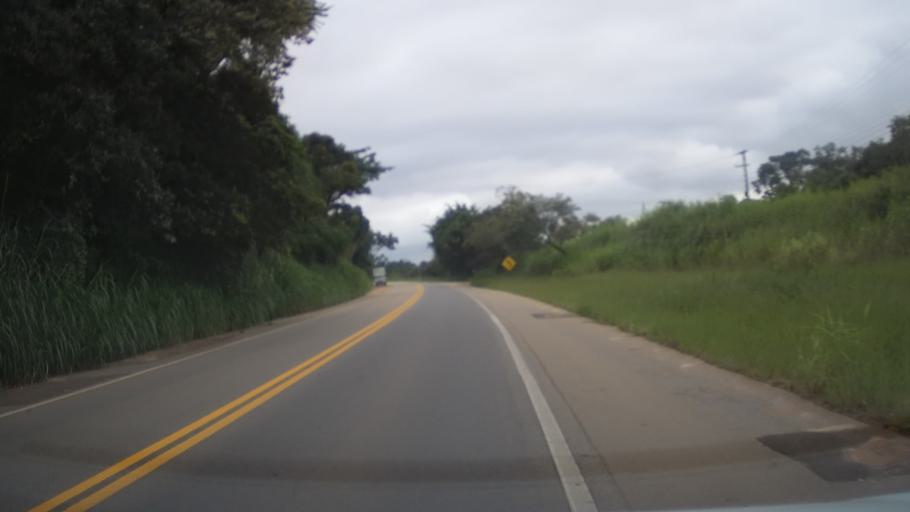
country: BR
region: Sao Paulo
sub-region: Louveira
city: Louveira
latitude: -23.1156
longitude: -46.9406
